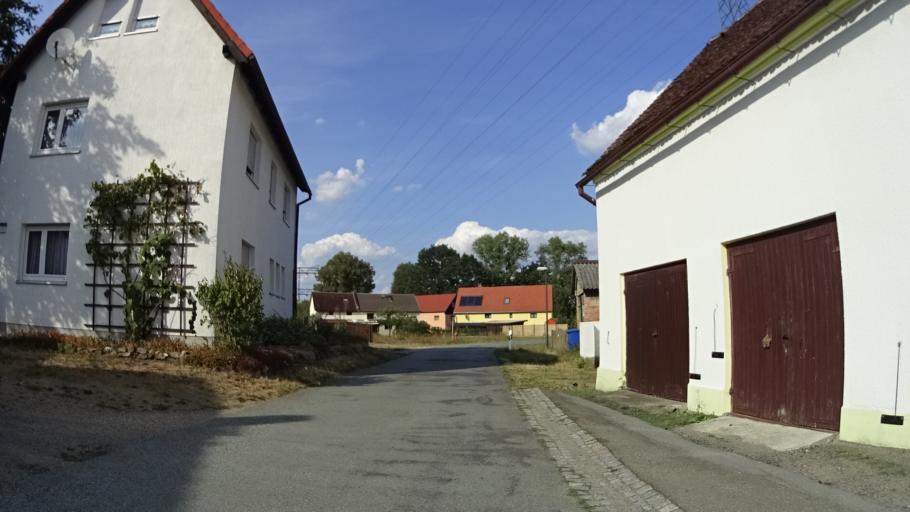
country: DE
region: Saxony
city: Ostritz
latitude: 51.0711
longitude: 14.9667
